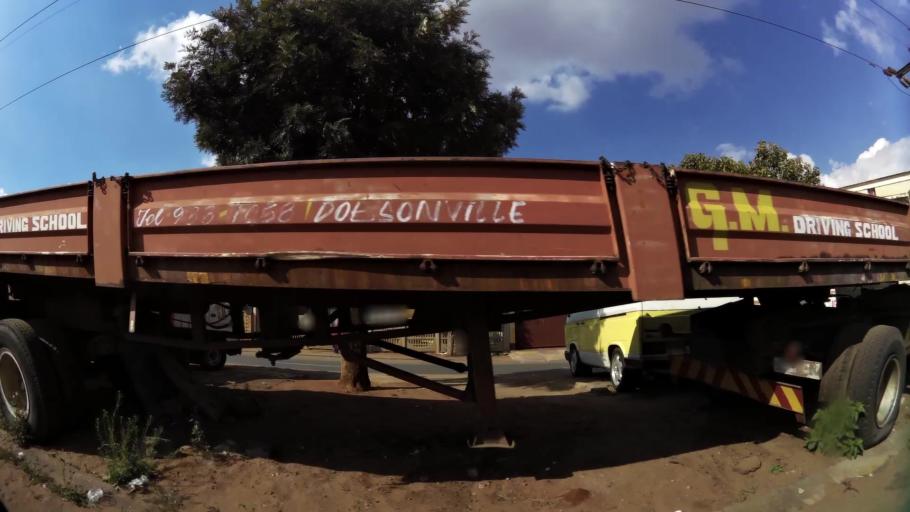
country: ZA
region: Gauteng
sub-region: City of Johannesburg Metropolitan Municipality
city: Soweto
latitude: -26.2217
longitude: 27.8580
